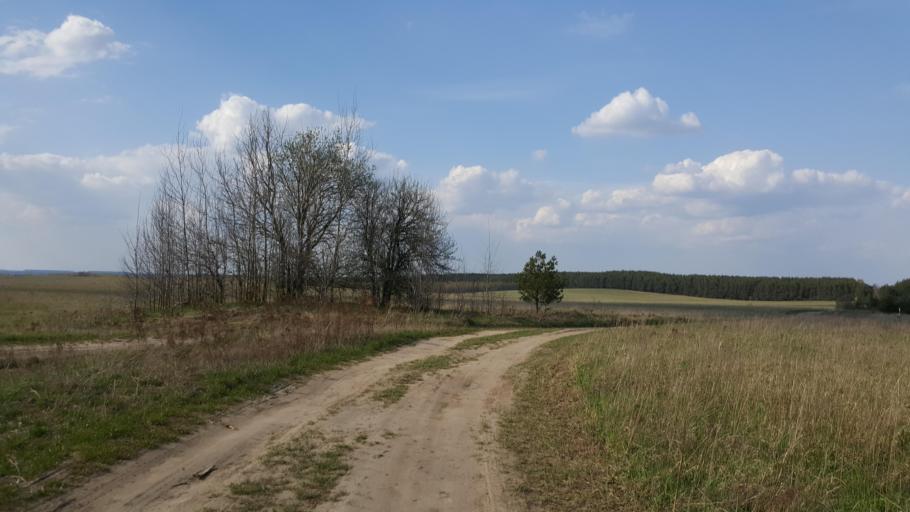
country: BY
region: Brest
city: Kamyanyets
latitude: 52.3724
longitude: 23.8353
